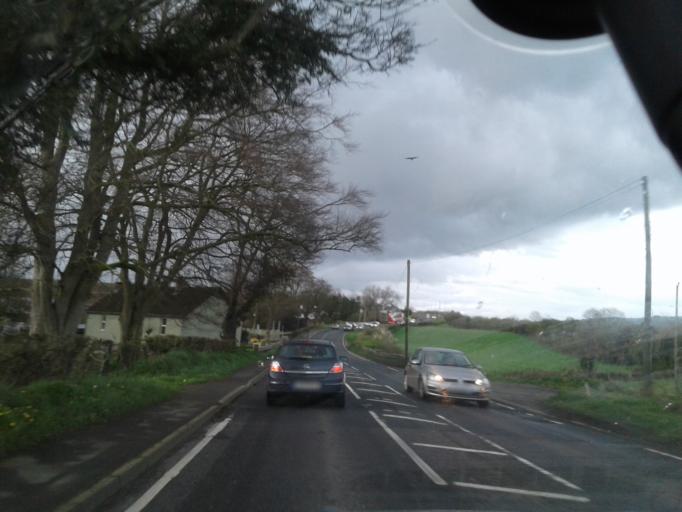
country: GB
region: Northern Ireland
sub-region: Strabane District
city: Sion Mills
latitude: 54.7979
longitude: -7.4753
